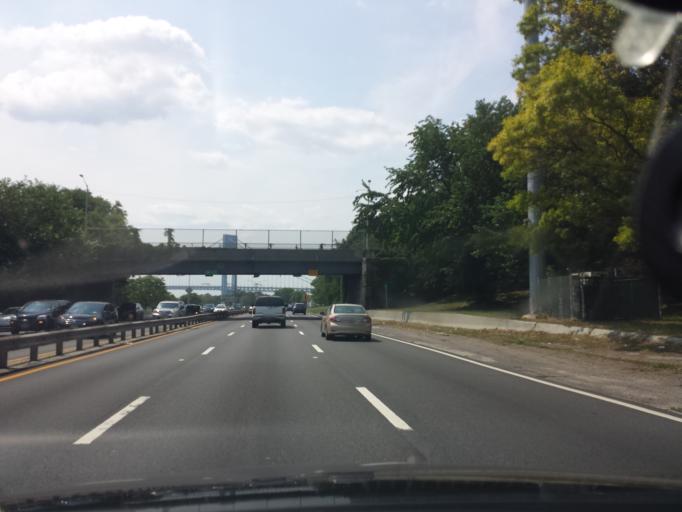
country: US
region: New York
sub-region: Kings County
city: Bensonhurst
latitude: 40.6036
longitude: -74.0185
